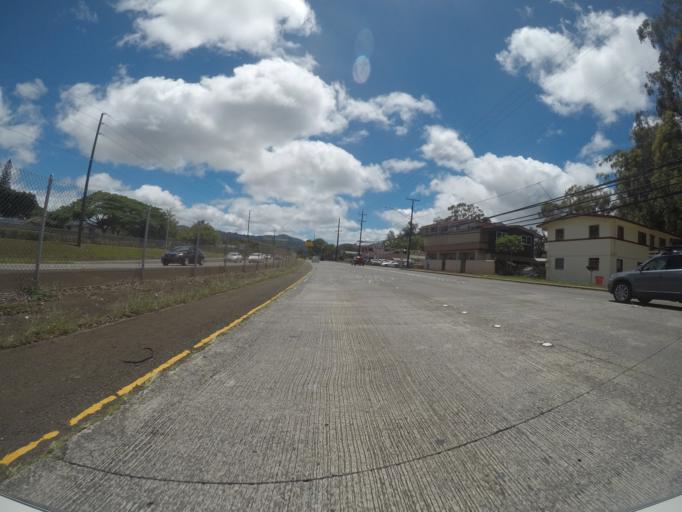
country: US
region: Hawaii
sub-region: Honolulu County
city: Wahiawa
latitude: 21.4904
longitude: -158.0318
